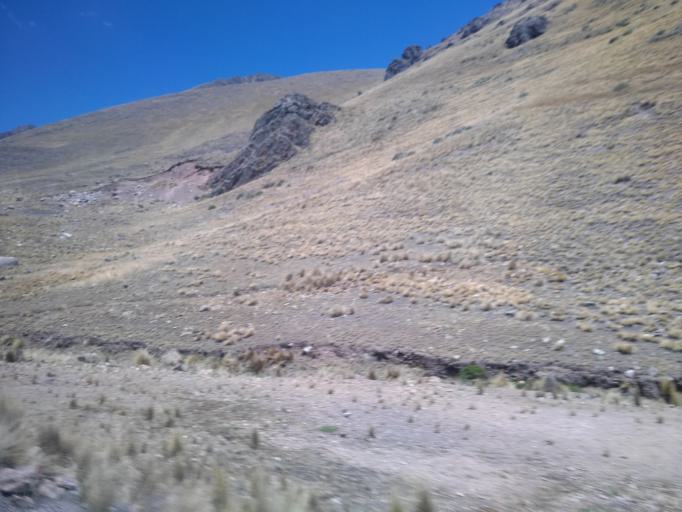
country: PE
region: Cusco
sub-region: Provincia de Canas
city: Layo
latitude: -14.4818
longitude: -71.0045
